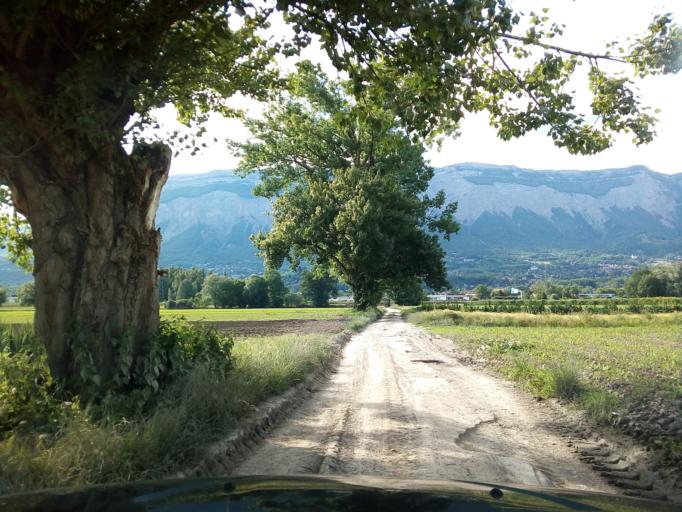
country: FR
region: Rhone-Alpes
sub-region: Departement de l'Isere
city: Montbonnot-Saint-Martin
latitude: 45.2137
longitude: 5.8190
